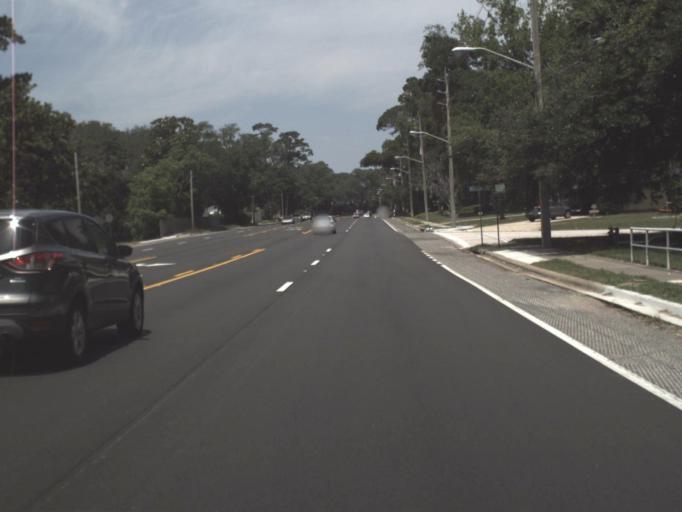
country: US
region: Florida
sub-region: Duval County
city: Jacksonville
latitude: 30.2465
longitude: -81.6312
